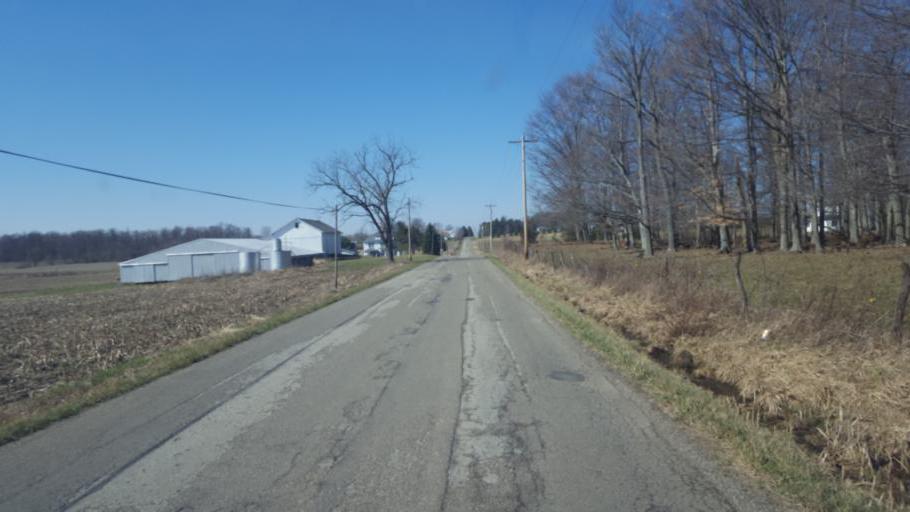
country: US
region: Ohio
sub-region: Morrow County
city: Mount Gilead
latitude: 40.5155
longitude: -82.7984
